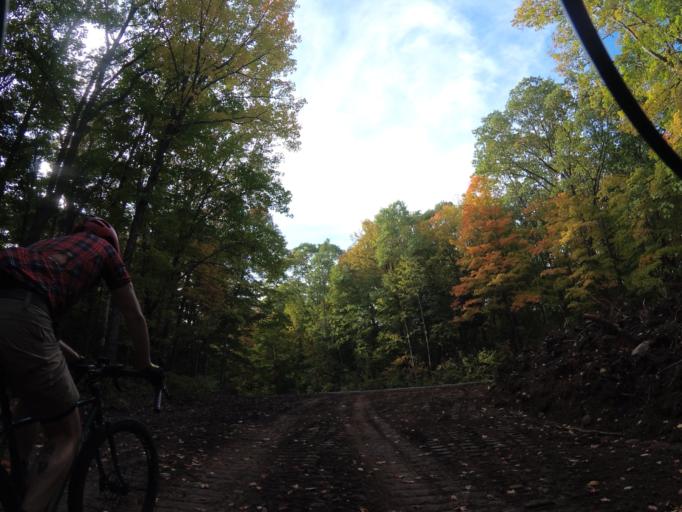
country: CA
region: Ontario
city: Pembroke
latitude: 45.3390
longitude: -77.1728
